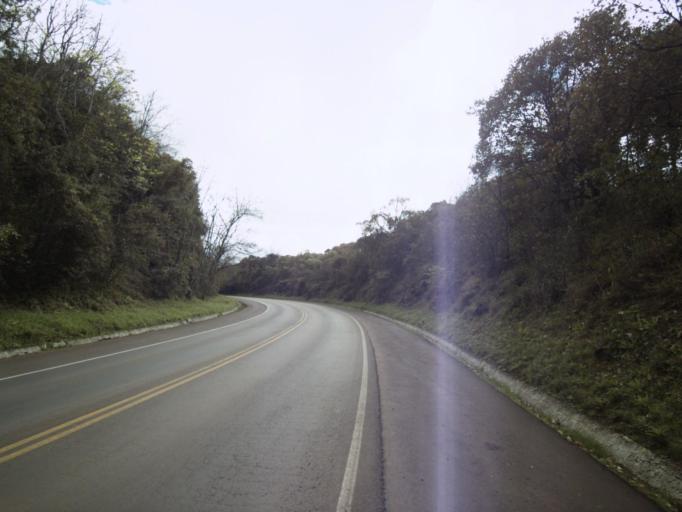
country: BR
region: Santa Catarina
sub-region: Concordia
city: Concordia
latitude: -27.2908
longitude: -51.9675
